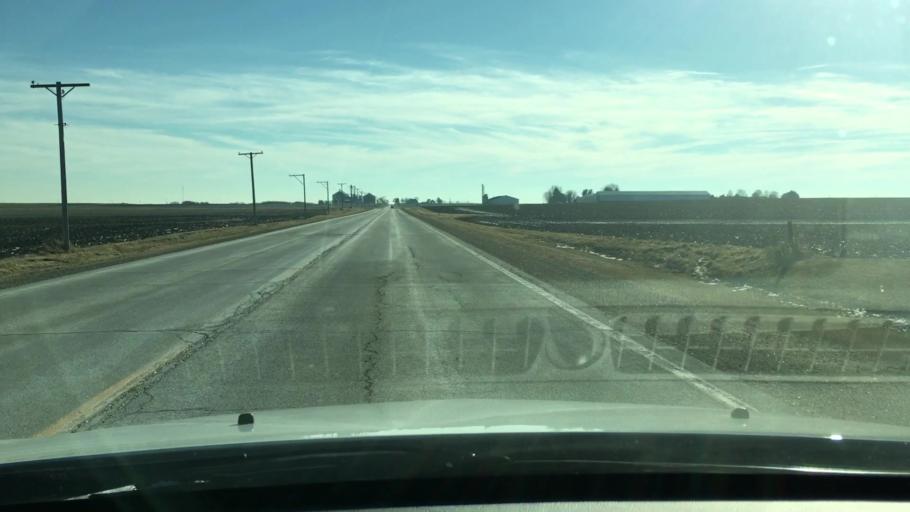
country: US
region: Illinois
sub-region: LaSalle County
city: Mendota
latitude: 41.6077
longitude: -89.1287
